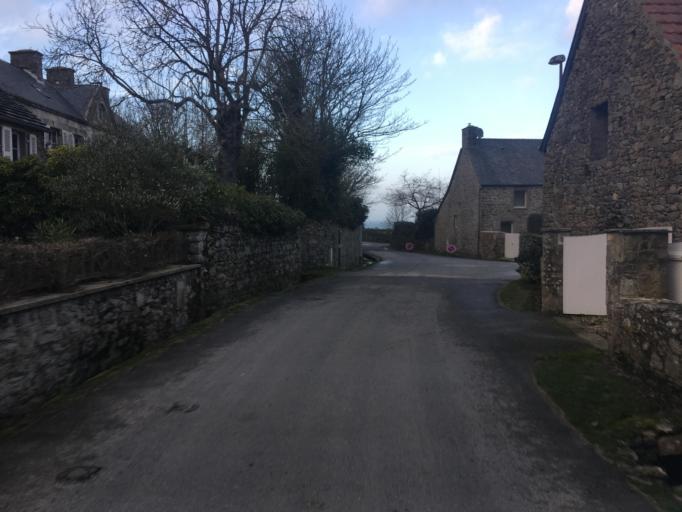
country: FR
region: Lower Normandy
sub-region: Departement de la Manche
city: Beaumont-Hague
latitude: 49.7141
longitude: -1.9221
